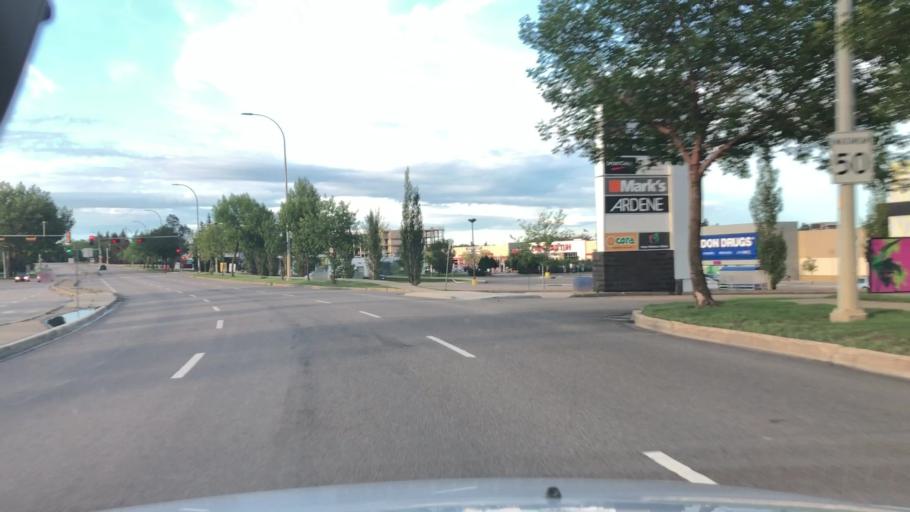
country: CA
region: Alberta
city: St. Albert
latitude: 53.6431
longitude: -113.6250
